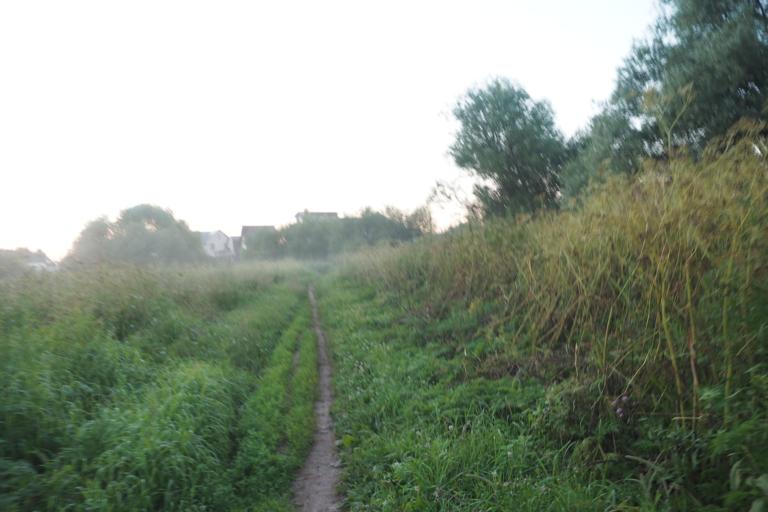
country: RU
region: Moskovskaya
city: Ramenskoye
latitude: 55.5503
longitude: 38.3010
